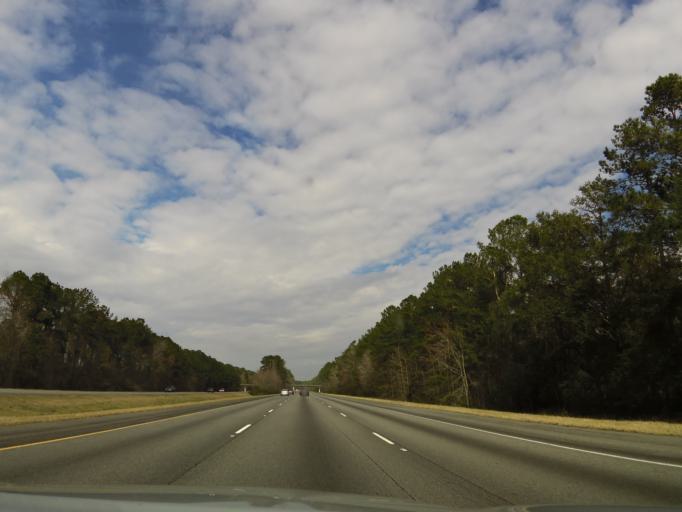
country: US
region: Georgia
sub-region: Bryan County
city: Richmond Hill
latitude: 31.8592
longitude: -81.3389
